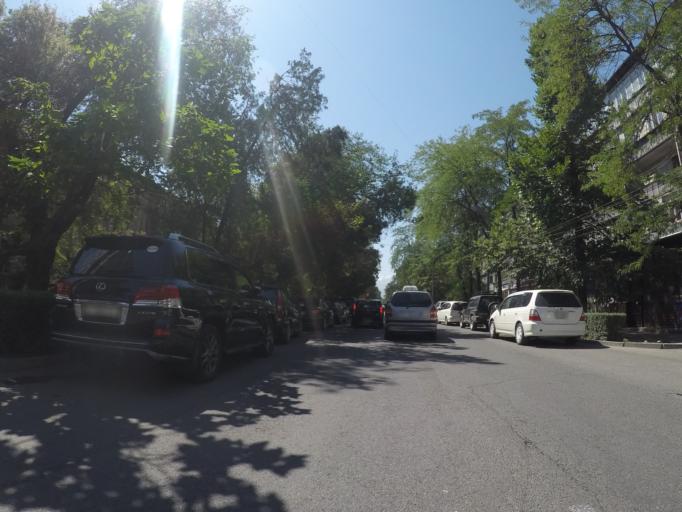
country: KG
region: Chuy
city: Bishkek
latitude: 42.8778
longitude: 74.5918
